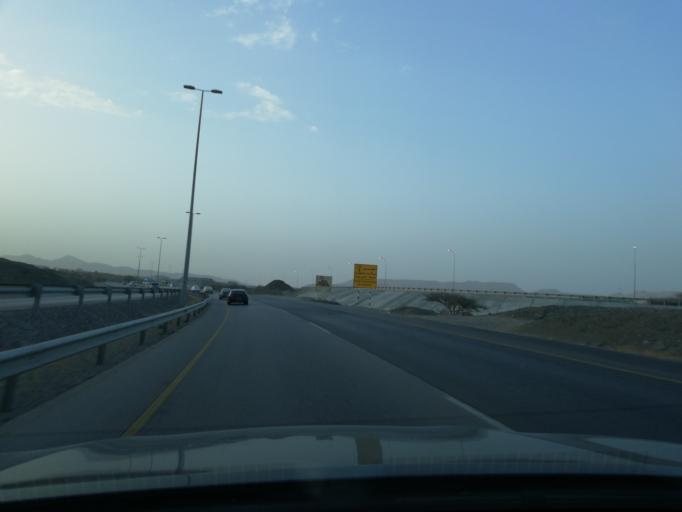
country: OM
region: Muhafazat ad Dakhiliyah
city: Bidbid
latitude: 23.4973
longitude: 58.1962
